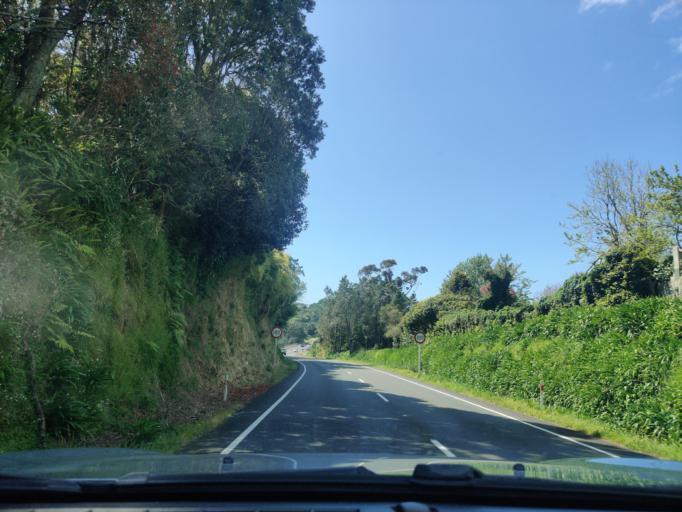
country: NZ
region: Taranaki
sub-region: New Plymouth District
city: New Plymouth
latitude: -39.1146
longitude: 173.9578
